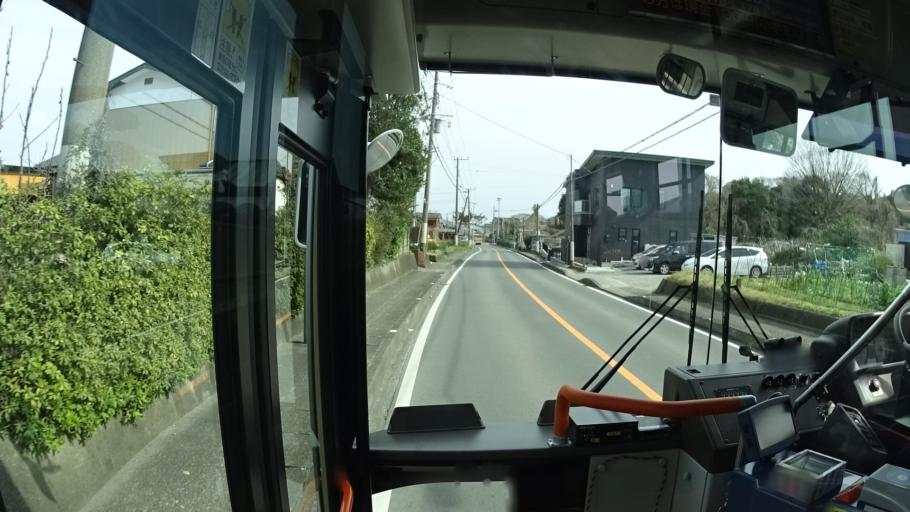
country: JP
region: Kanagawa
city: Zama
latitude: 35.5120
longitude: 139.3014
